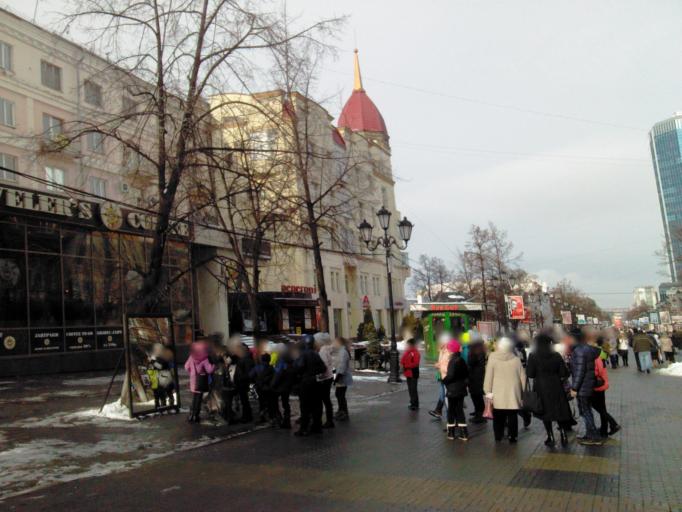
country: RU
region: Chelyabinsk
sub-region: Gorod Chelyabinsk
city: Chelyabinsk
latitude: 55.1619
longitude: 61.4009
